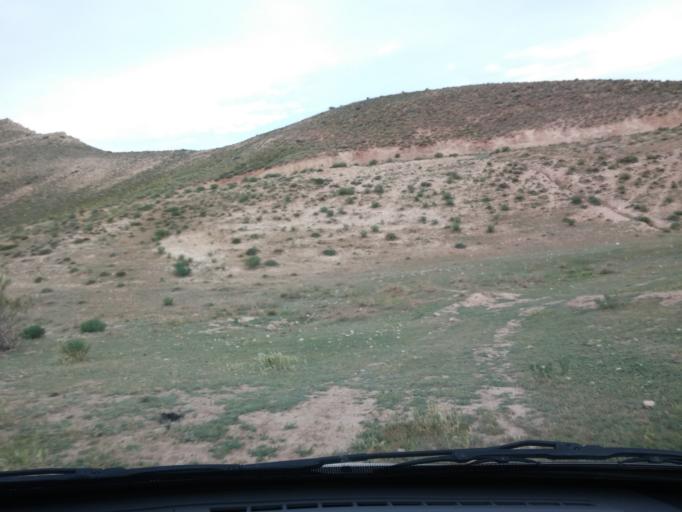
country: IR
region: Semnan
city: Istgah-e Rah Ahan-e Garmsar
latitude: 35.4728
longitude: 52.2884
